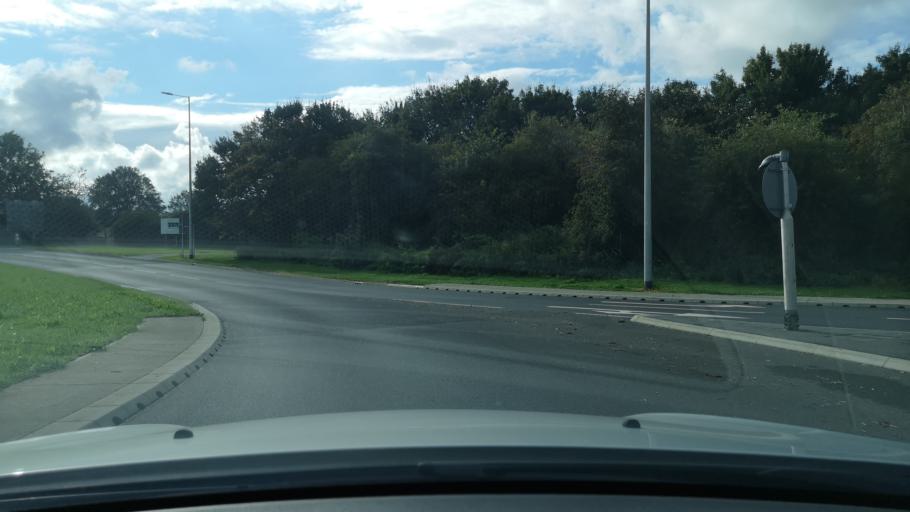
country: GB
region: England
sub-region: East Riding of Yorkshire
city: Walkington
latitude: 53.8428
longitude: -0.4777
